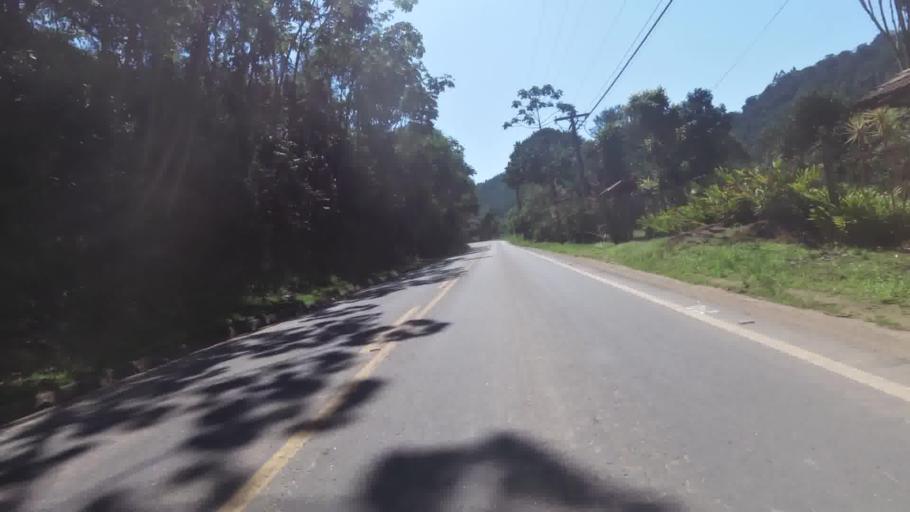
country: BR
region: Espirito Santo
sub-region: Marechal Floriano
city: Marechal Floriano
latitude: -20.4512
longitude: -40.7856
